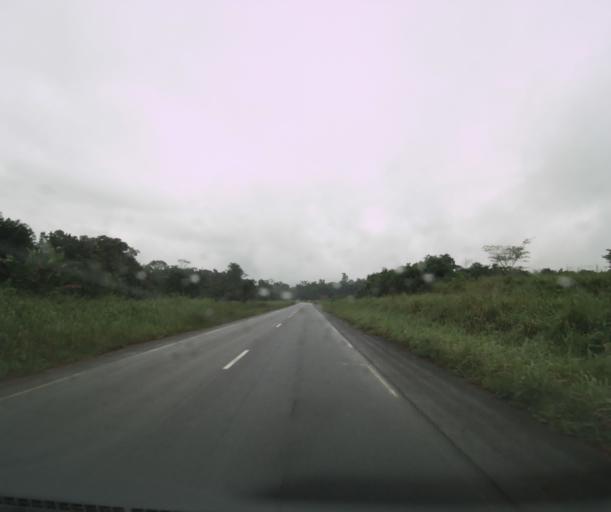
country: CM
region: Littoral
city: Edea
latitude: 3.4658
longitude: 10.1314
